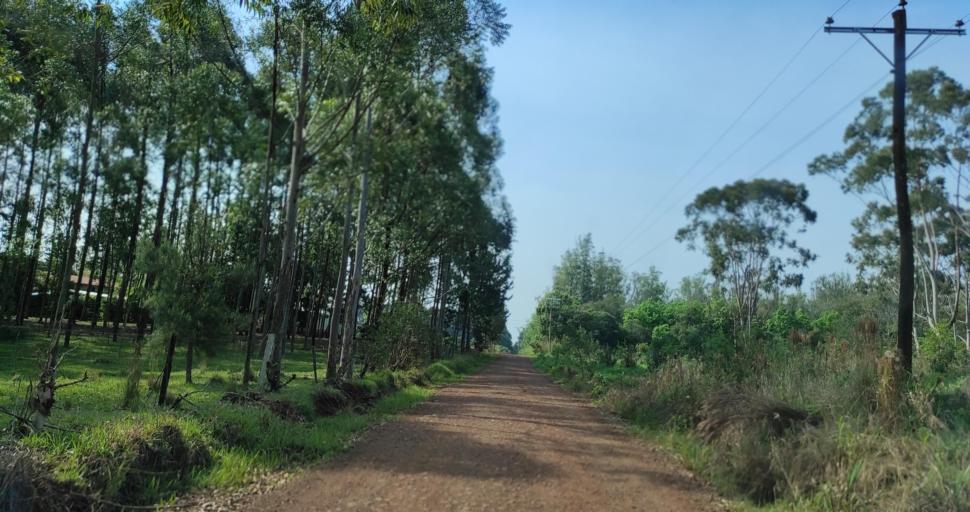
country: AR
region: Misiones
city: Capiovi
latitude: -26.8850
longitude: -55.0484
